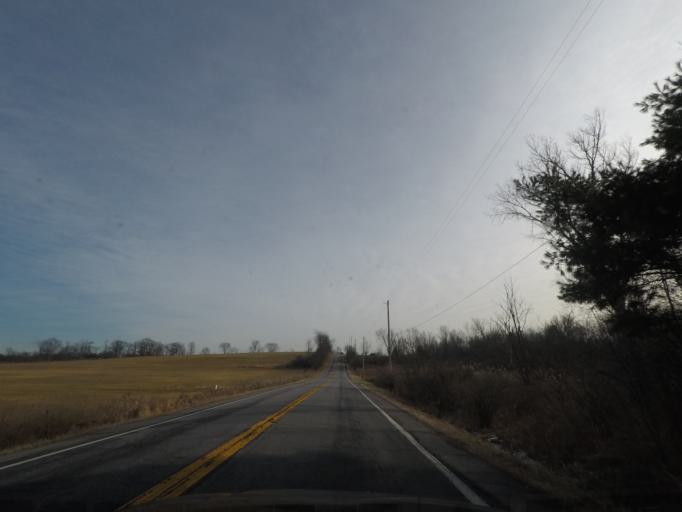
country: US
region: New York
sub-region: Saratoga County
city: Stillwater
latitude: 42.9858
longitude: -73.6544
